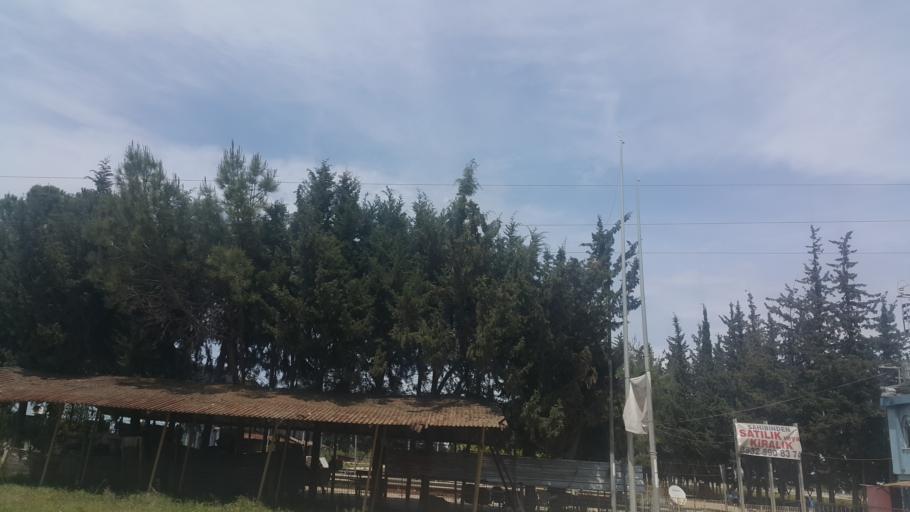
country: TR
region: Adana
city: Yuregir
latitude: 36.9757
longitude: 35.4871
